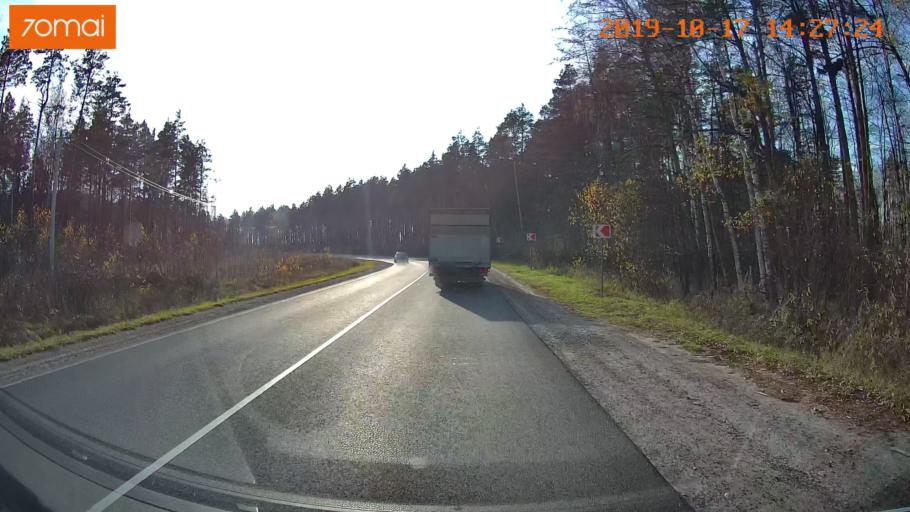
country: RU
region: Moskovskaya
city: Radovitskiy
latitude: 54.9866
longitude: 39.9540
